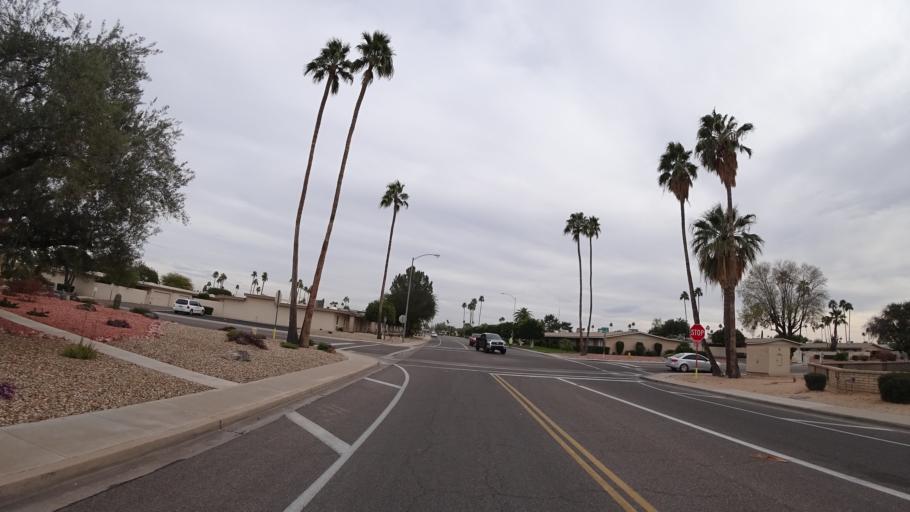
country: US
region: Arizona
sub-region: Maricopa County
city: Youngtown
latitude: 33.6091
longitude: -112.2975
